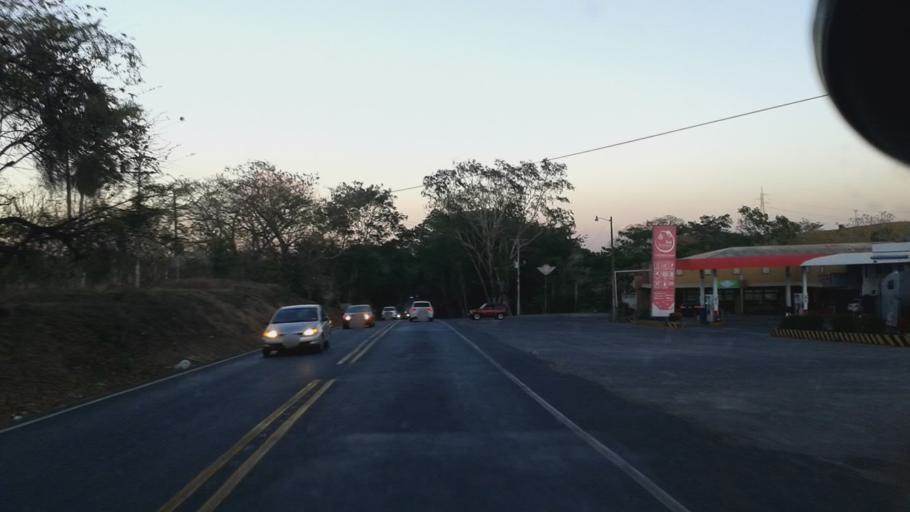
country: CR
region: Puntarenas
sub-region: Canton Central de Puntarenas
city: Puntarenas
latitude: 10.1112
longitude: -84.8899
